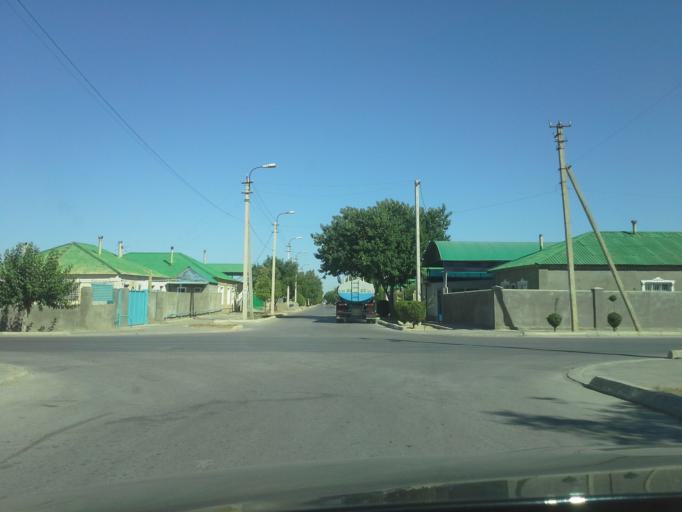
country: TM
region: Ahal
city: Abadan
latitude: 38.0806
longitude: 58.1572
